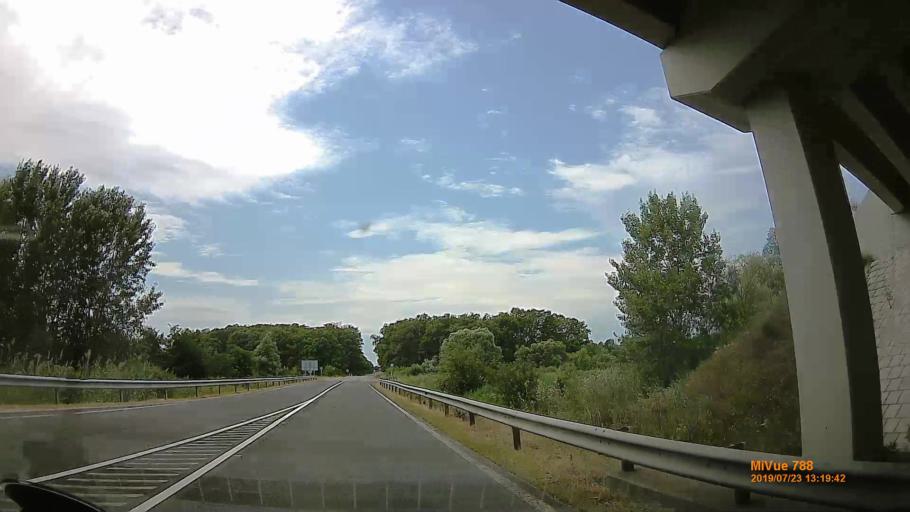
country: HU
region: Hajdu-Bihar
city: Polgar
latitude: 47.8723
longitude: 21.1369
